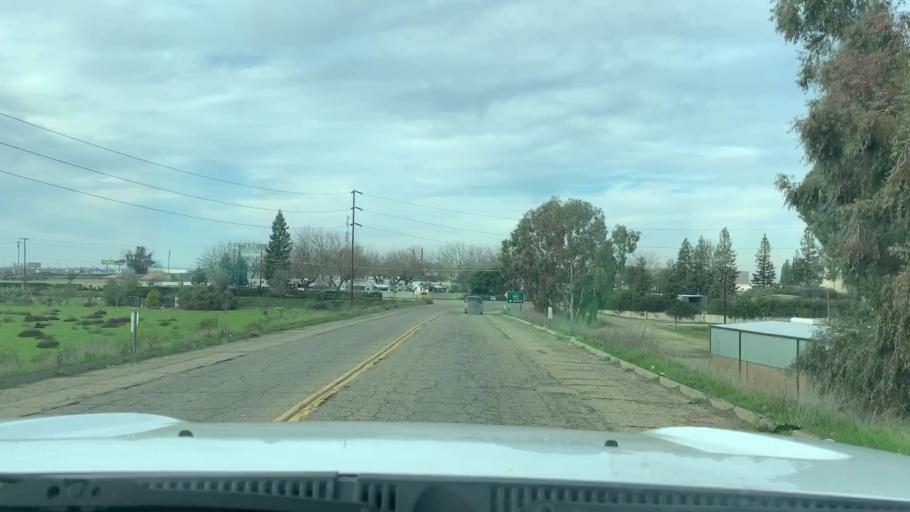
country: US
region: California
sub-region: Fresno County
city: Kingsburg
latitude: 36.5312
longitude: -119.5758
